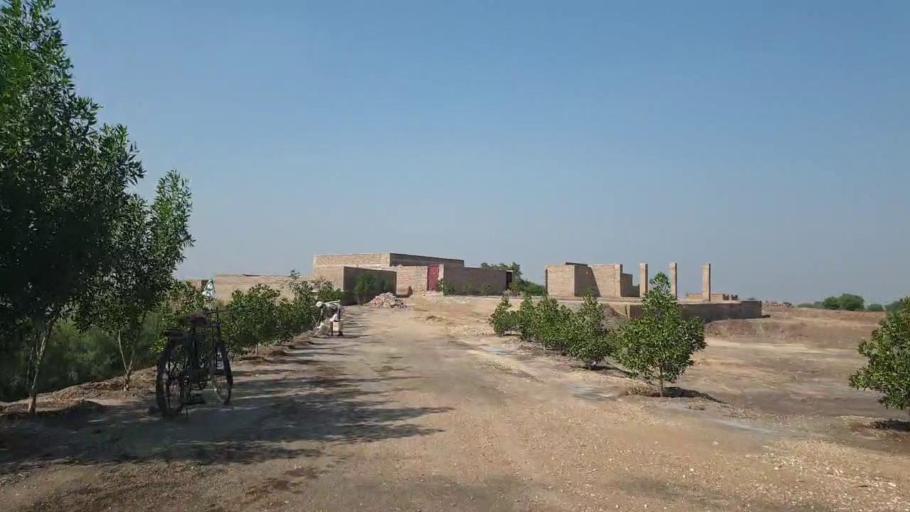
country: PK
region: Sindh
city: Sehwan
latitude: 26.4264
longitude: 67.8330
